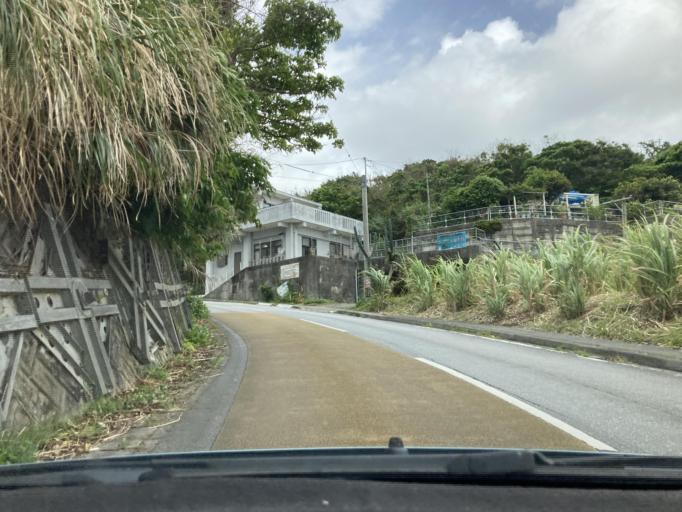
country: JP
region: Okinawa
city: Ginowan
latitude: 26.2291
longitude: 127.7444
